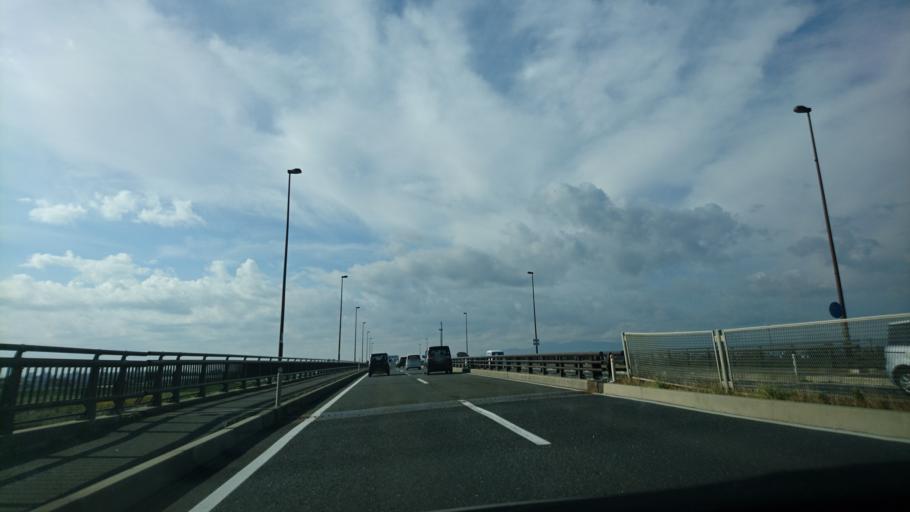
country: JP
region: Miyagi
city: Furukawa
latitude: 38.5961
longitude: 140.9670
